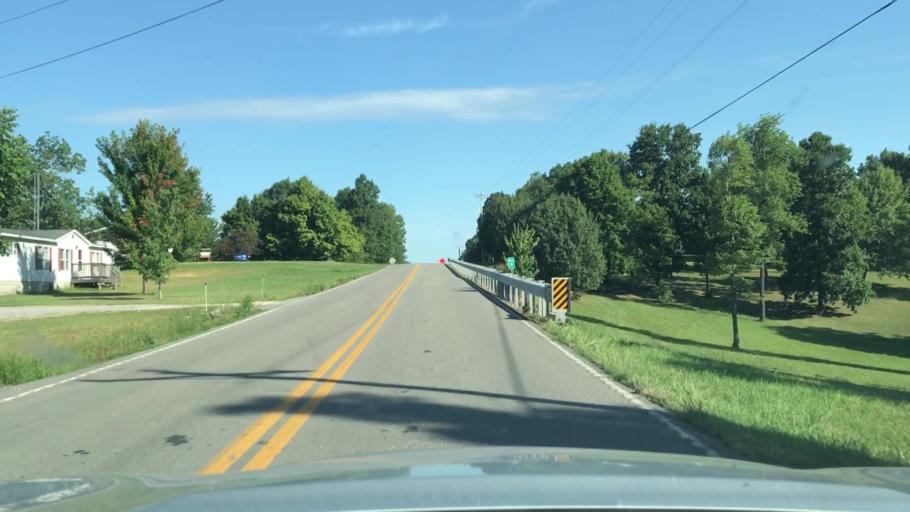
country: US
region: Kentucky
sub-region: Muhlenberg County
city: Greenville
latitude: 37.1151
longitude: -87.1291
